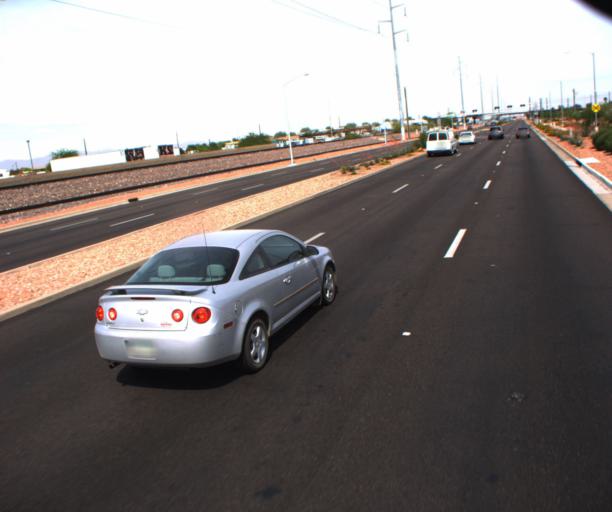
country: US
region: Arizona
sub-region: Maricopa County
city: Glendale
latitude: 33.5486
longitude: -112.1977
